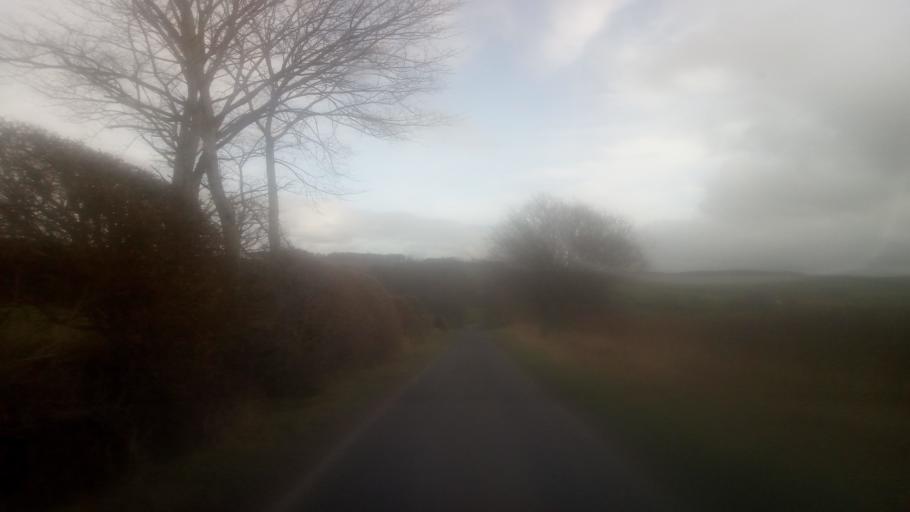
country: GB
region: Scotland
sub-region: The Scottish Borders
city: Jedburgh
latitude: 55.4872
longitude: -2.4958
